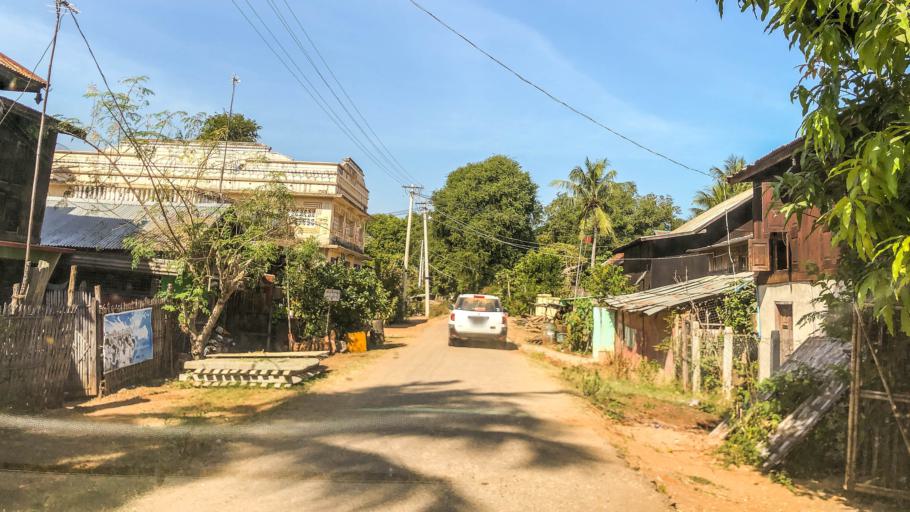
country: MM
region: Magway
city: Magway
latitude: 19.9737
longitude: 95.0393
